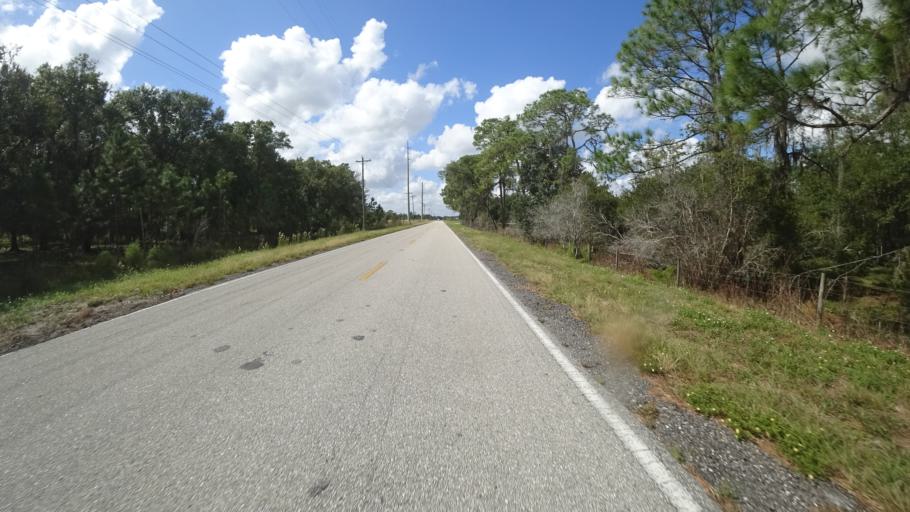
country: US
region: Florida
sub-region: Hardee County
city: Wauchula
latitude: 27.4582
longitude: -82.0906
